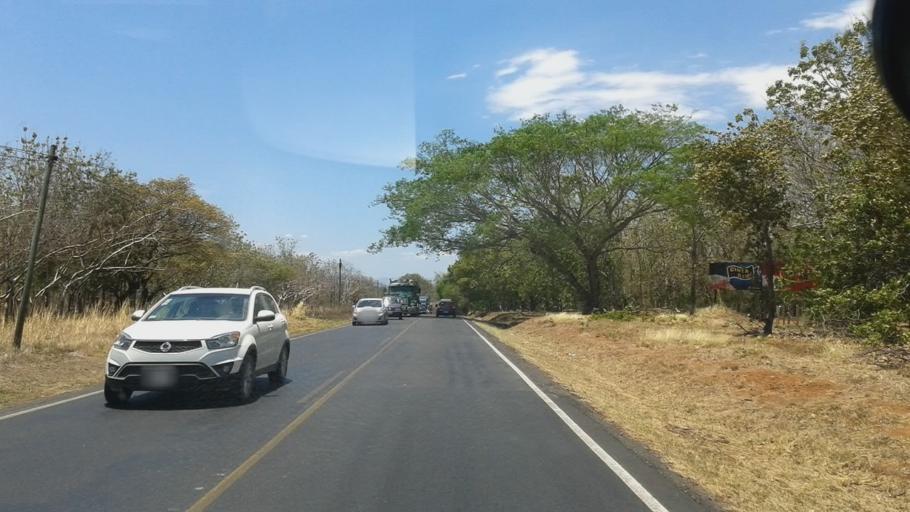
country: CR
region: Puntarenas
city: Miramar
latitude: 10.0890
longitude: -84.8322
